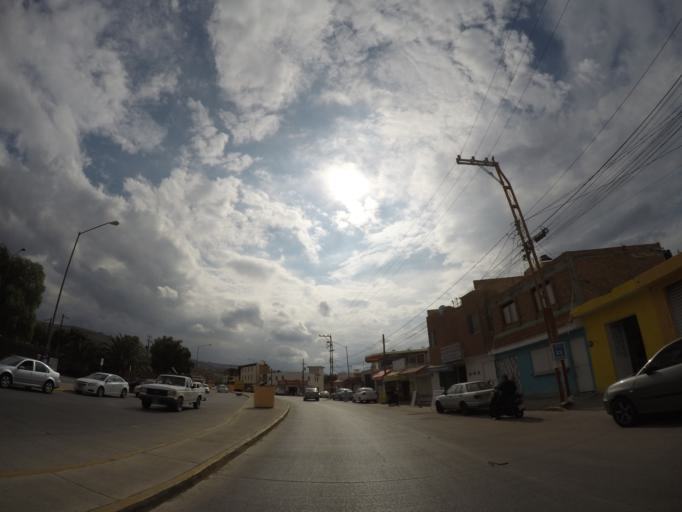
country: MX
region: San Luis Potosi
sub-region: San Luis Potosi
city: San Luis Potosi
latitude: 22.1247
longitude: -100.9840
